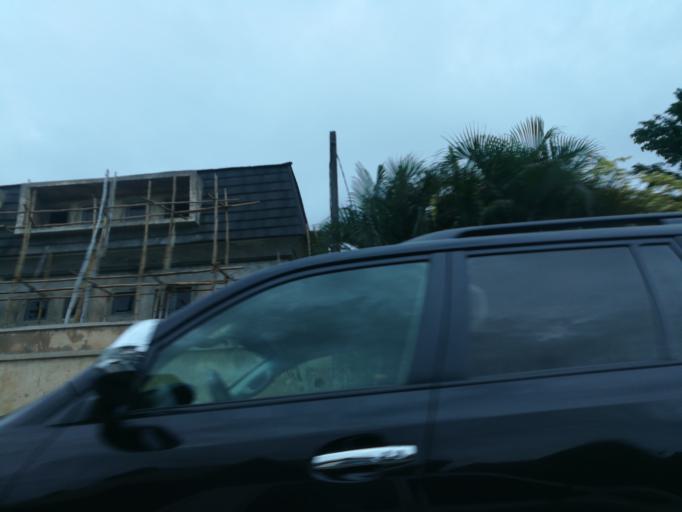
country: NG
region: Lagos
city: Ikoyi
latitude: 6.4419
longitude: 3.4714
